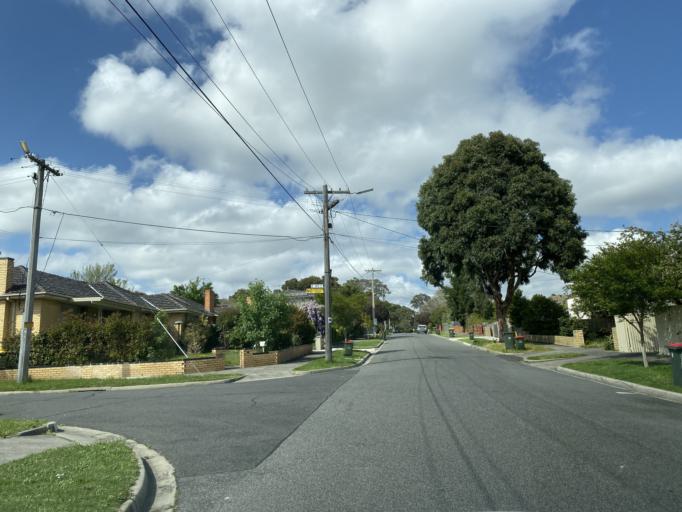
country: AU
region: Victoria
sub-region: Whitehorse
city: Burwood
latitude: -37.8457
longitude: 145.1264
